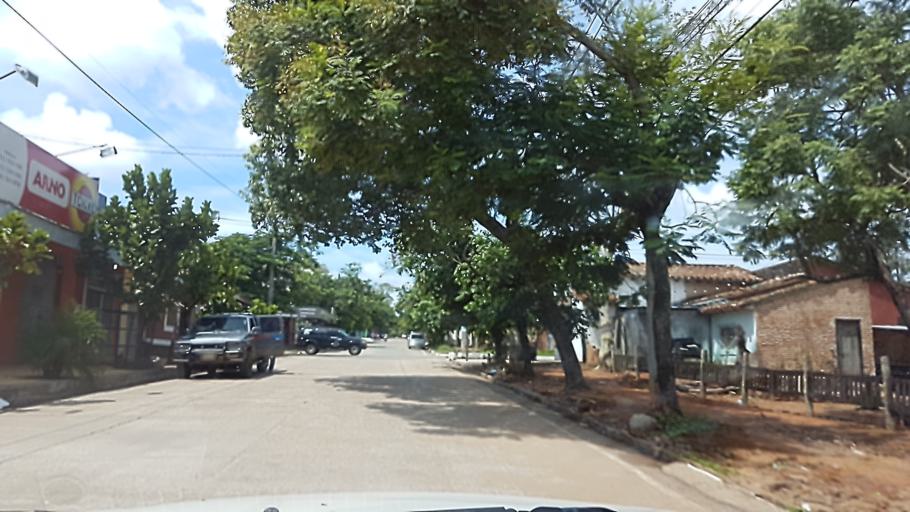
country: PY
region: Central
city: Limpio
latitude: -25.1674
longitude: -57.4757
